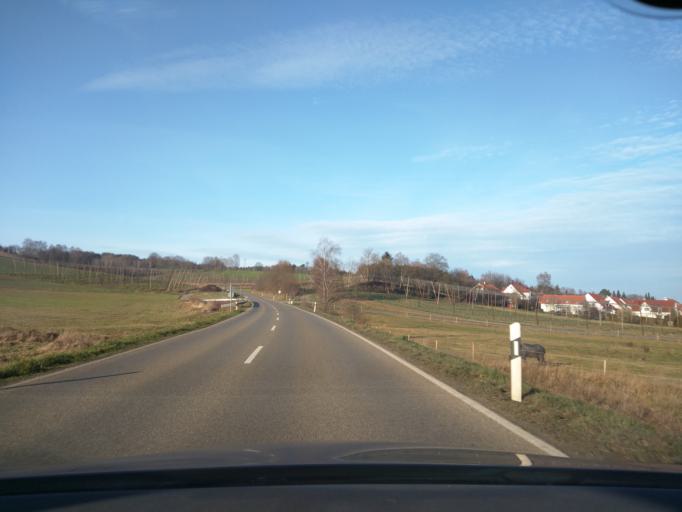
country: DE
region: Bavaria
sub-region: Upper Bavaria
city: Wolnzach
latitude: 48.6074
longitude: 11.6139
